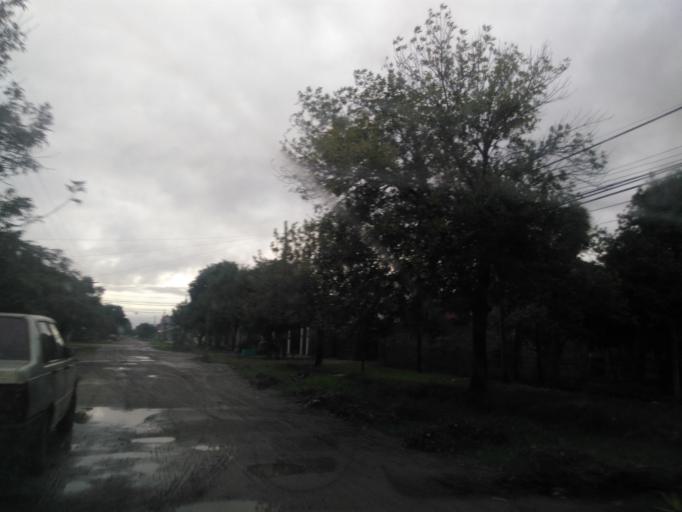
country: AR
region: Chaco
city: Resistencia
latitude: -27.4691
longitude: -59.0030
